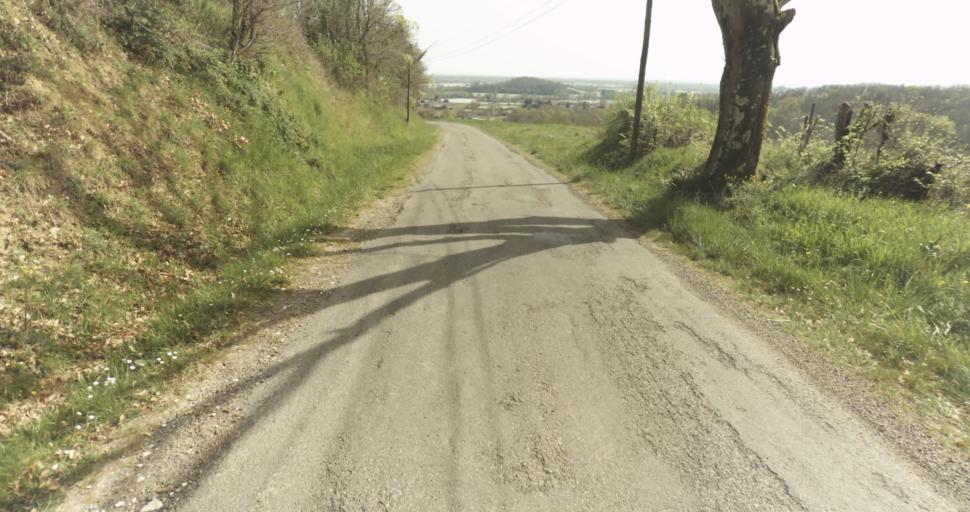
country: FR
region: Midi-Pyrenees
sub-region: Departement du Tarn-et-Garonne
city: Moissac
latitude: 44.1329
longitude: 1.1472
